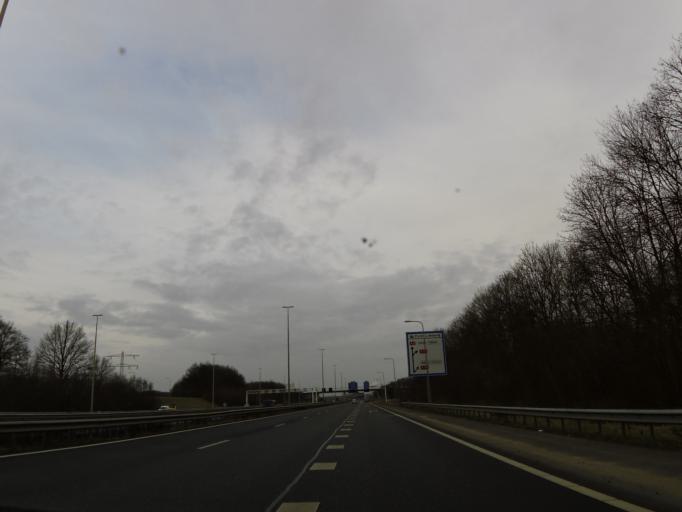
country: NL
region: Limburg
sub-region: Gemeente Stein
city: Elsloo
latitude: 50.9603
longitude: 5.7868
